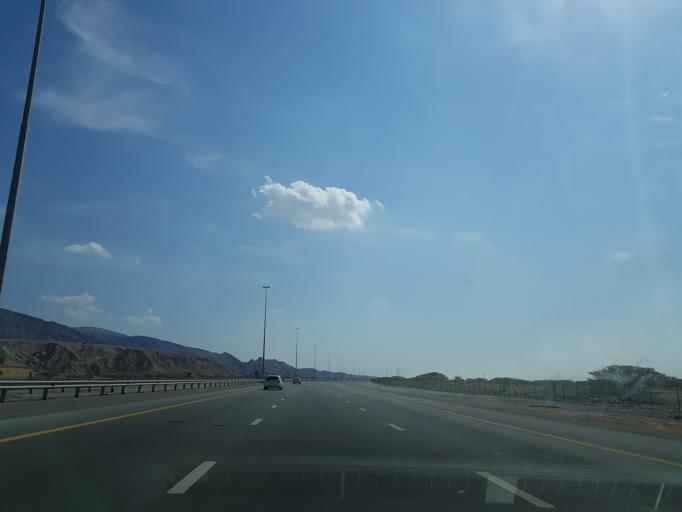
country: AE
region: Ra's al Khaymah
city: Ras al-Khaimah
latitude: 25.7881
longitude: 56.0312
